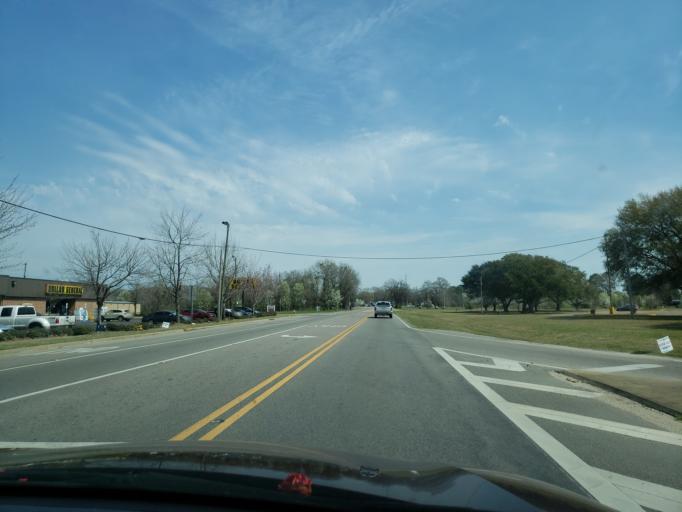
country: US
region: Alabama
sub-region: Autauga County
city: Prattville
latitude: 32.4364
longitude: -86.4777
